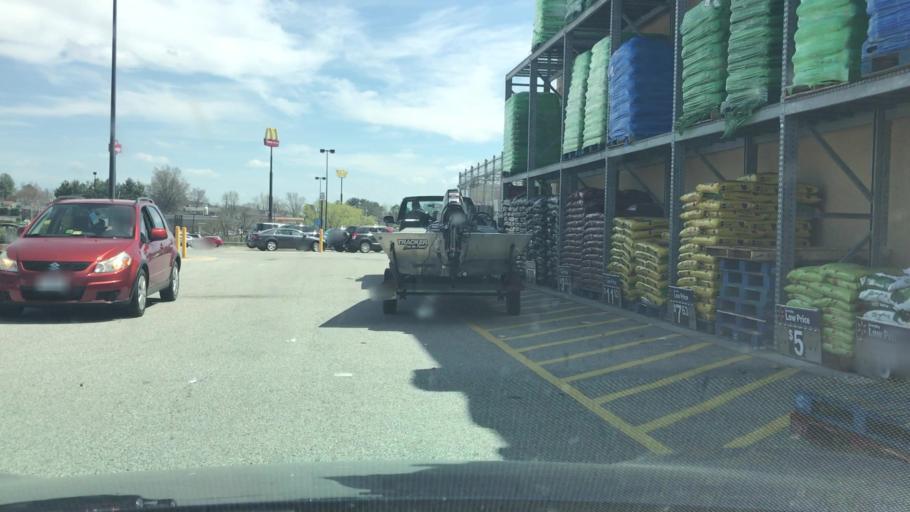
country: US
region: Virginia
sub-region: Pulaski County
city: Dublin
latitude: 37.0844
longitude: -80.6935
